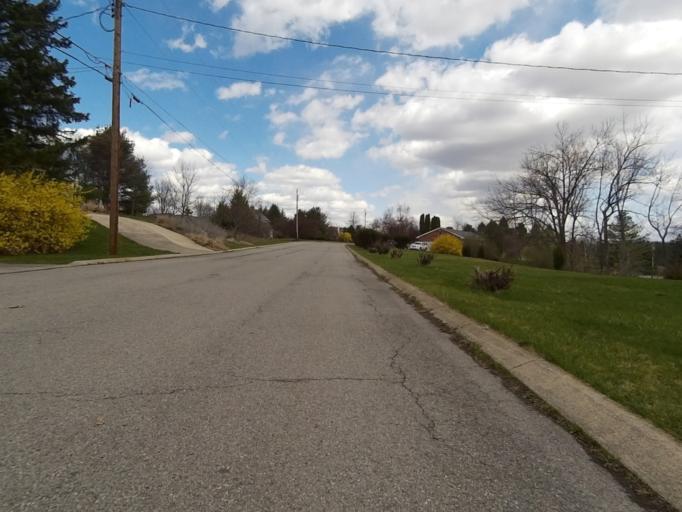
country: US
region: Pennsylvania
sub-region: Centre County
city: Park Forest Village
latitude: 40.8288
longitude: -77.9476
